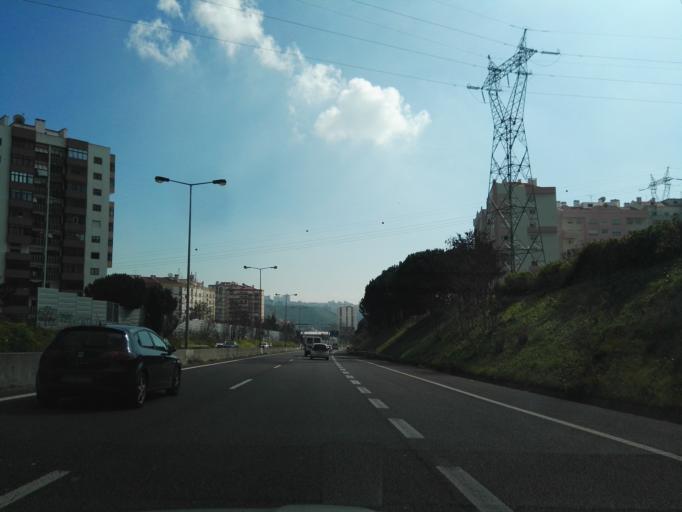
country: PT
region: Lisbon
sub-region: Odivelas
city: Povoa de Santo Adriao
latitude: 38.7995
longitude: -9.1757
